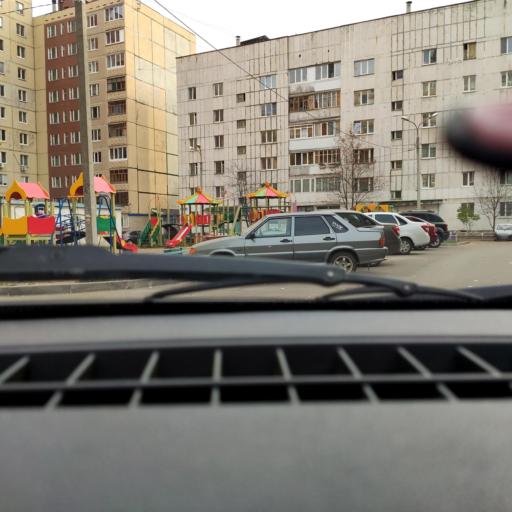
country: RU
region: Bashkortostan
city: Ufa
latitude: 54.7964
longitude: 56.0550
